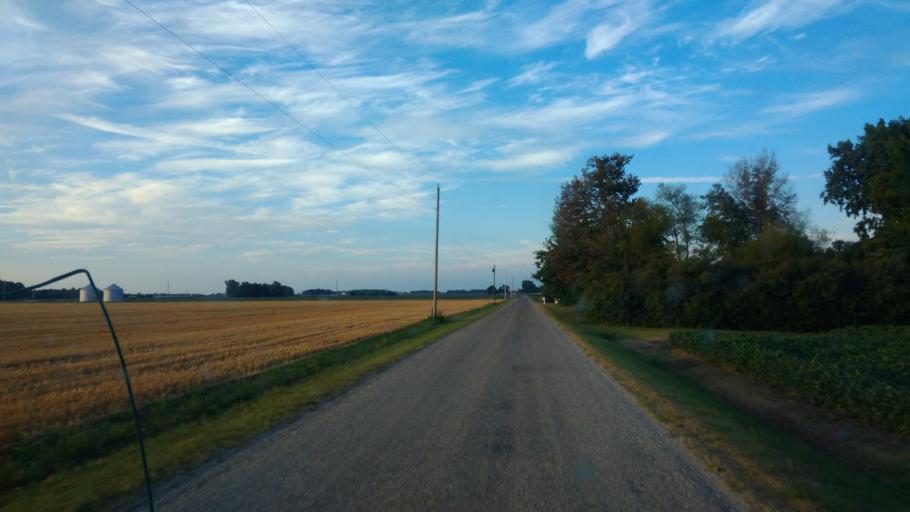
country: US
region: Indiana
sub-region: Adams County
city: Berne
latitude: 40.6440
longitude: -85.0606
